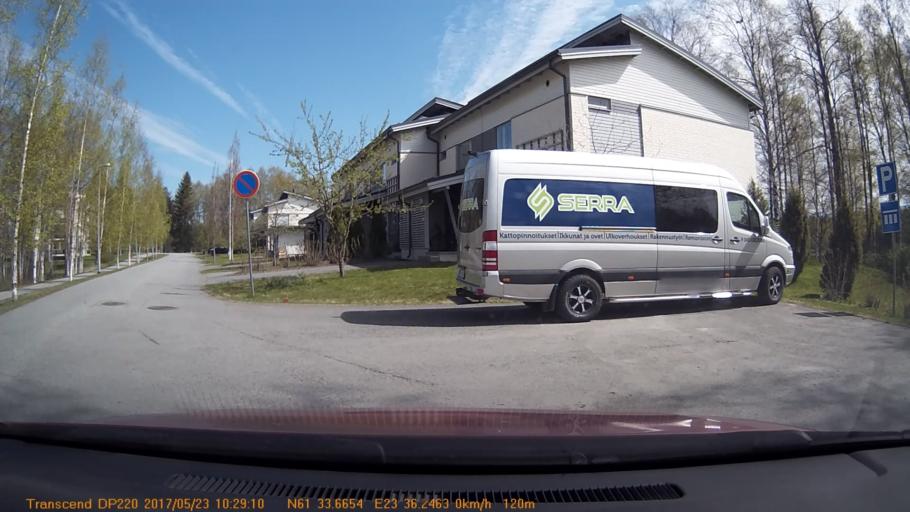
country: FI
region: Pirkanmaa
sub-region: Tampere
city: Yloejaervi
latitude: 61.5611
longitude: 23.6041
